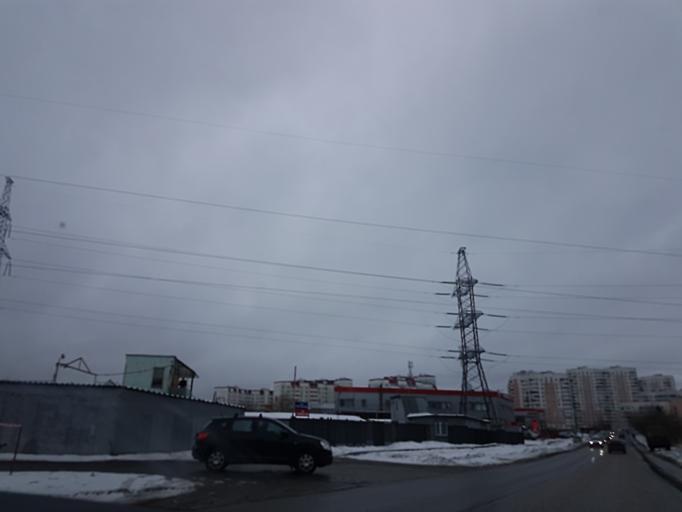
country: RU
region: Moskovskaya
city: Pavshino
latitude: 55.8248
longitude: 37.3549
